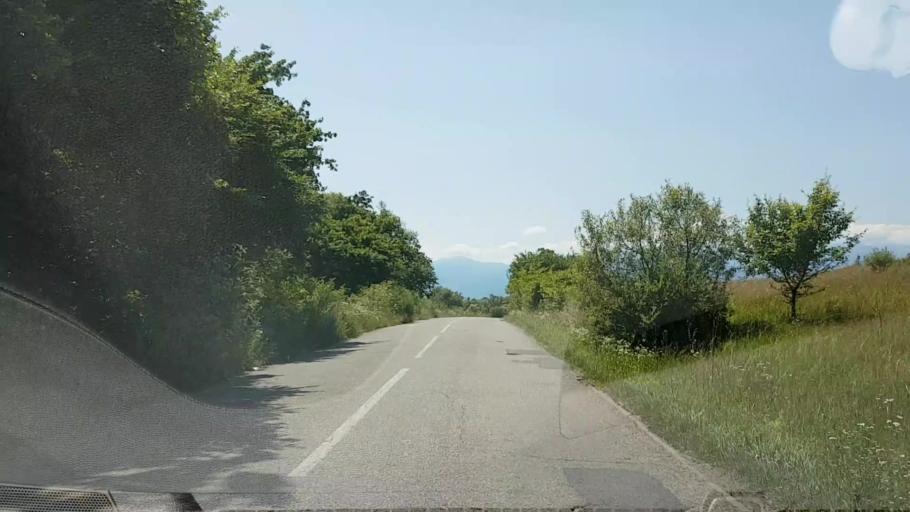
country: RO
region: Brasov
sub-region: Comuna Voila
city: Voila
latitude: 45.8655
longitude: 24.8250
